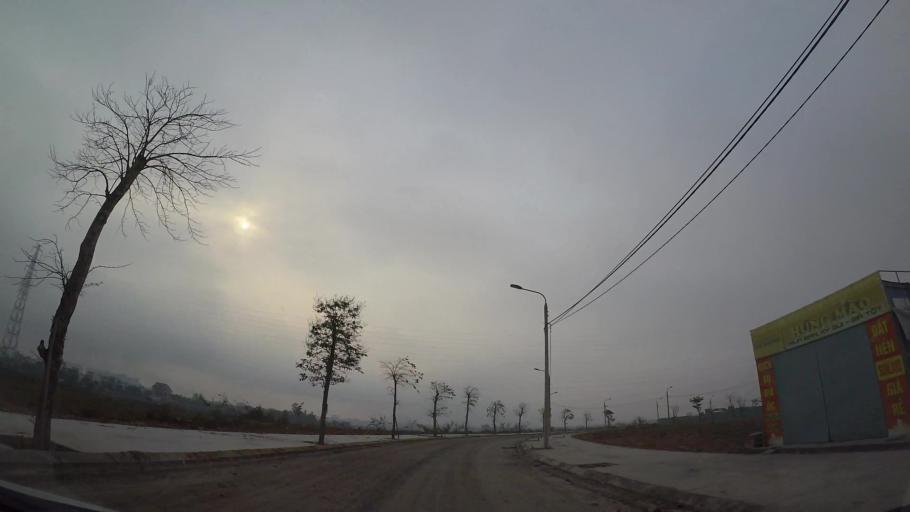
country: VN
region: Da Nang
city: Ngu Hanh Son
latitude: 16.0229
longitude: 108.2373
